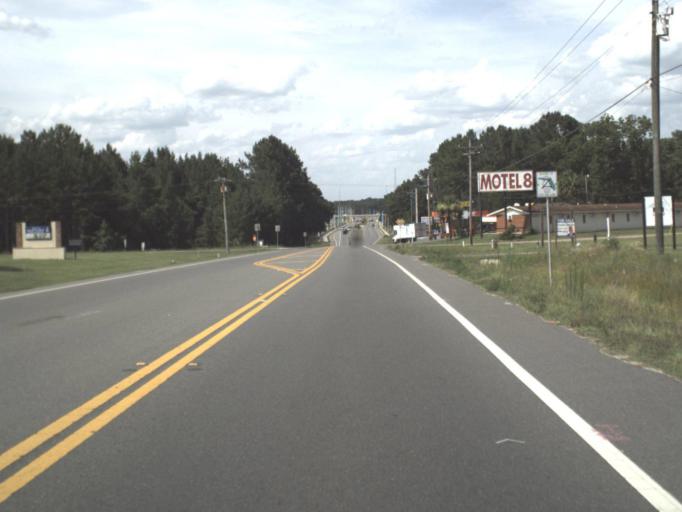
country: US
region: Florida
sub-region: Columbia County
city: Lake City
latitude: 30.1088
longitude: -82.6607
